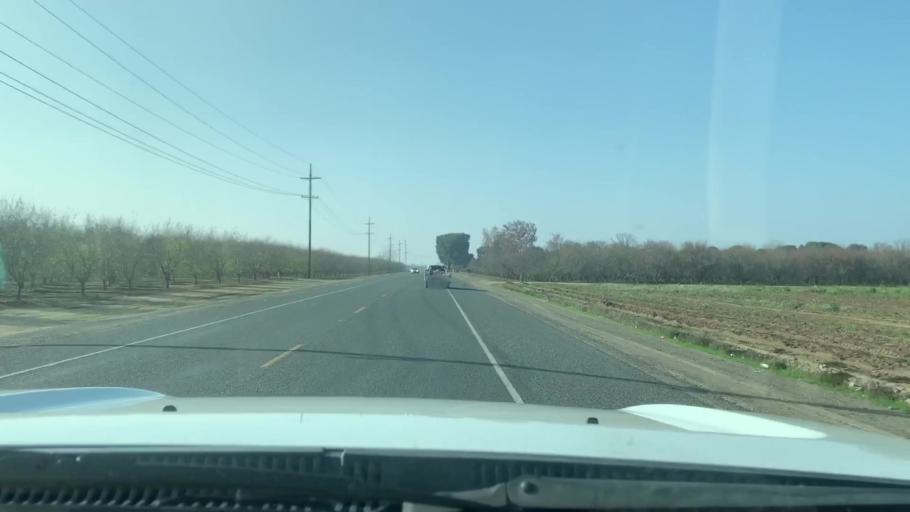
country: US
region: California
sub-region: Kern County
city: Wasco
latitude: 35.6015
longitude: -119.3792
